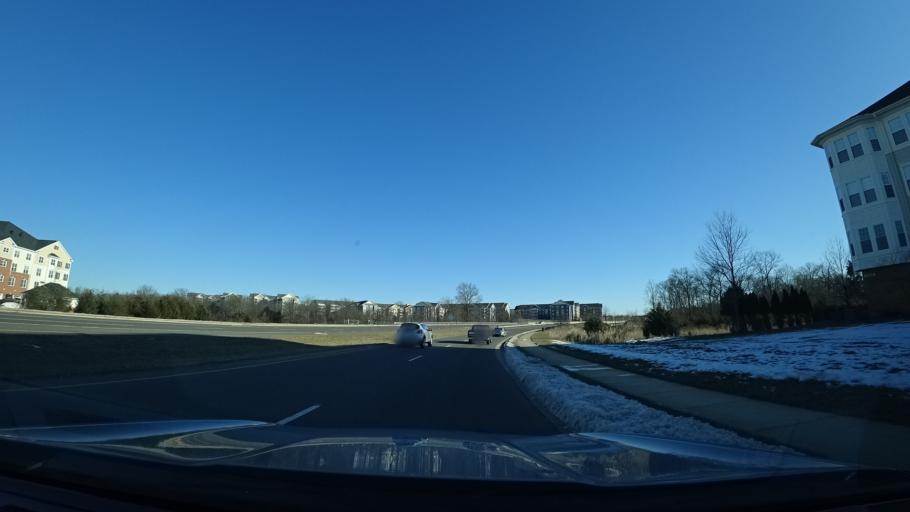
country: US
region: Virginia
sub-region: Loudoun County
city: University Center
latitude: 39.0339
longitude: -77.4599
